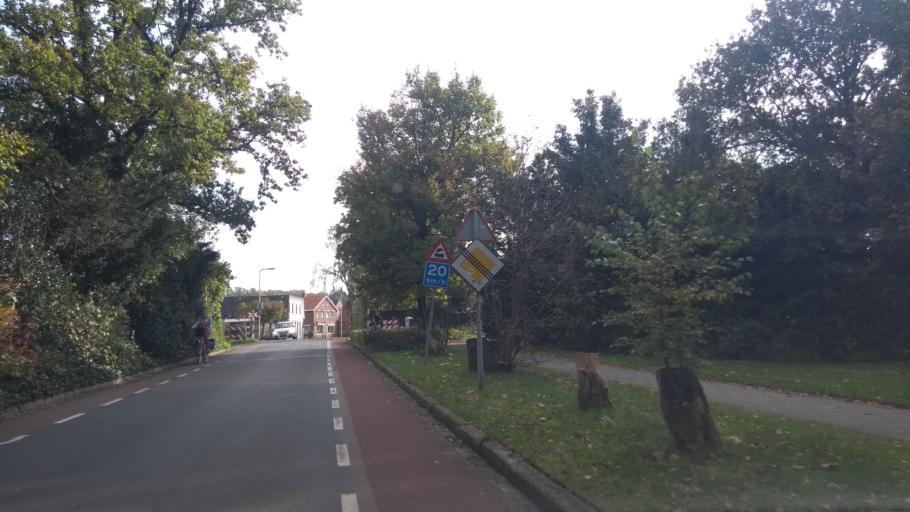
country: NL
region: Overijssel
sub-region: Gemeente Haaksbergen
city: Haaksbergen
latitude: 52.1658
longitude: 6.7501
